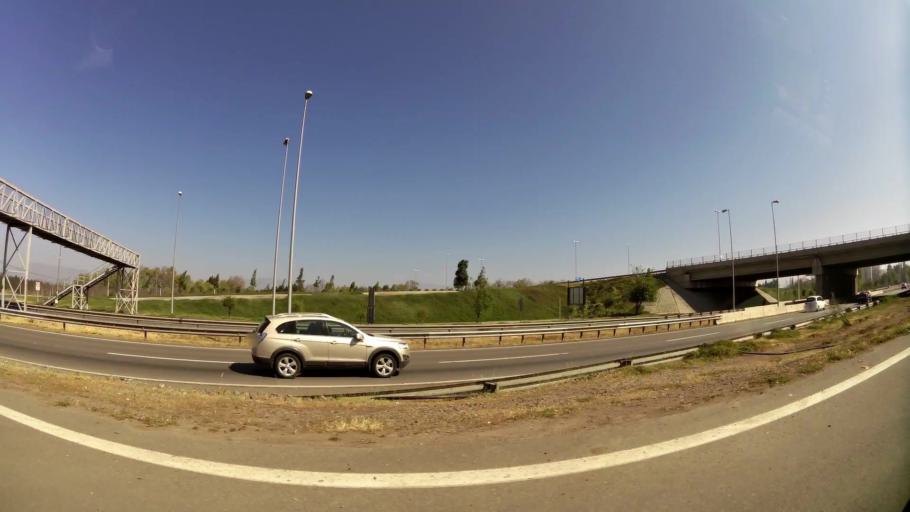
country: CL
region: Santiago Metropolitan
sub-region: Provincia de Chacabuco
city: Chicureo Abajo
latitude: -33.2922
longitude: -70.7017
